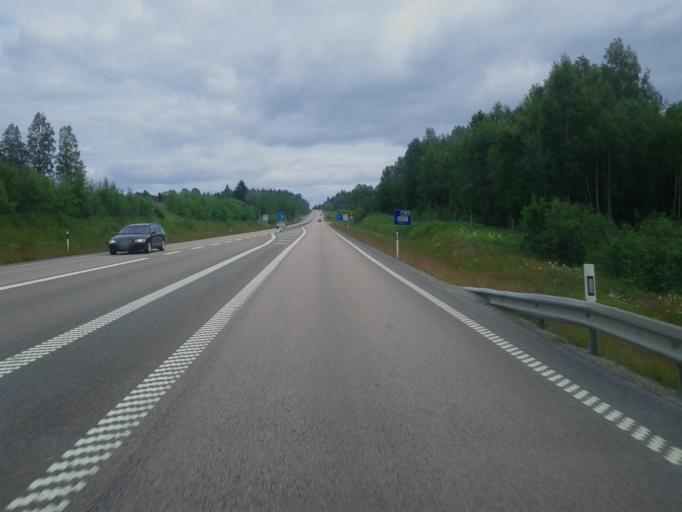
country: SE
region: Vaesternorrland
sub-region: OErnskoeldsviks Kommun
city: Bjasta
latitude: 63.1770
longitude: 18.4404
